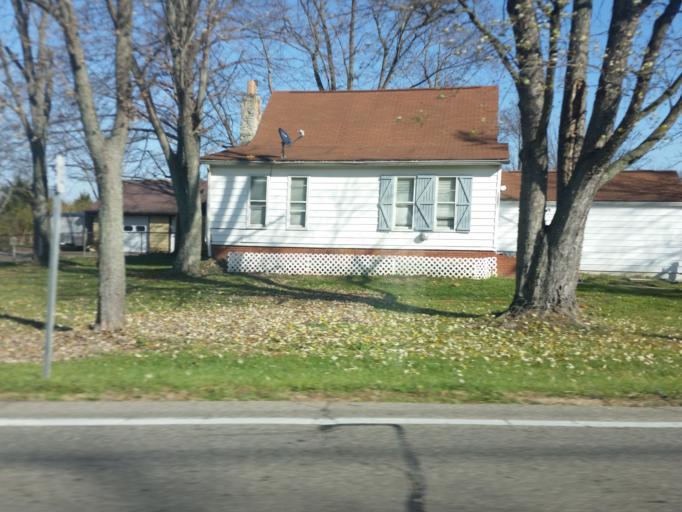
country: US
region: Ohio
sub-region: Butler County
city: Oxford
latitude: 39.4641
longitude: -84.6977
